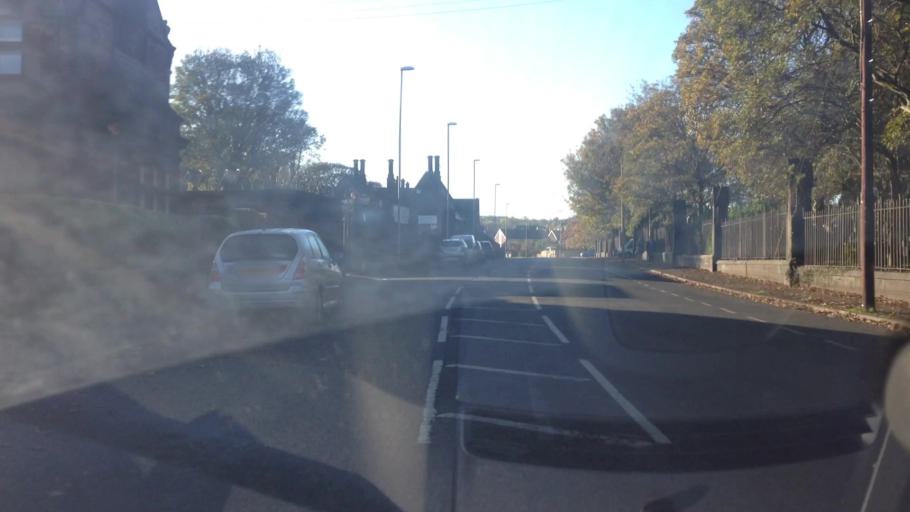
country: GB
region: England
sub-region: City and Borough of Leeds
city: Leeds
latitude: 53.7697
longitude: -1.5238
